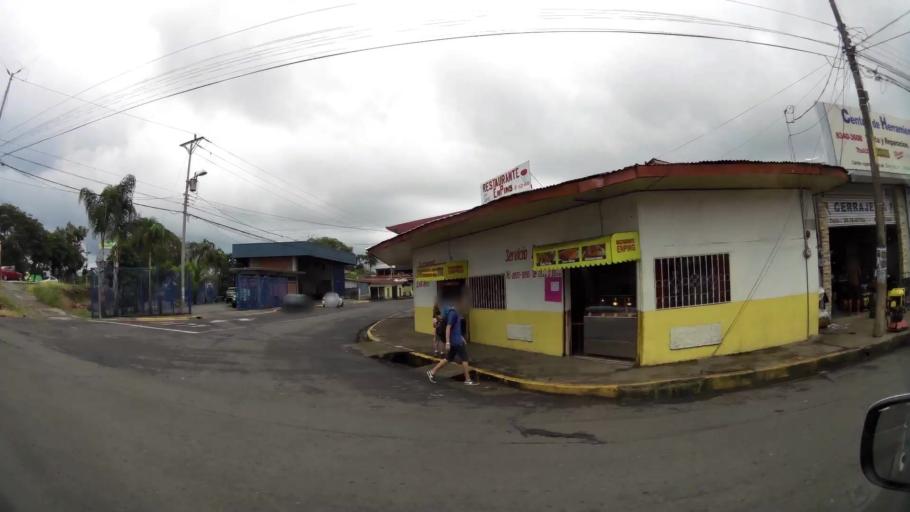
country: CR
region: Puntarenas
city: Esparza
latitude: 9.9948
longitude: -84.6653
